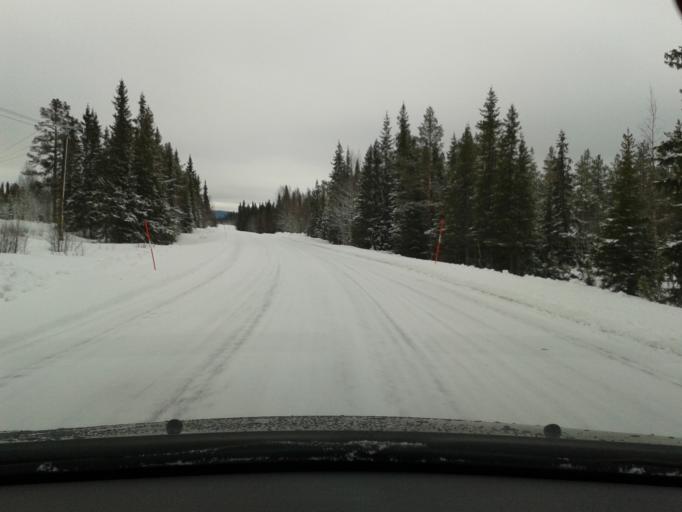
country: SE
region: Vaesterbotten
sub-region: Vilhelmina Kommun
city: Sjoberg
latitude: 65.2253
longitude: 15.9250
